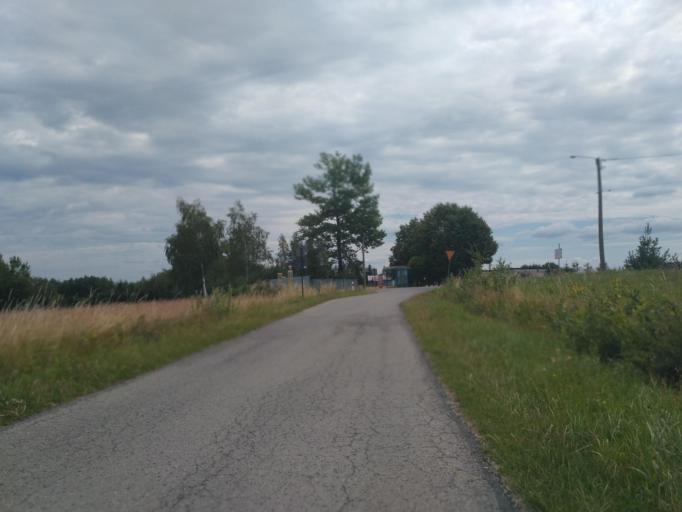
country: PL
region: Subcarpathian Voivodeship
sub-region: Powiat rzeszowski
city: Straszydle
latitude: 49.8820
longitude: 21.9866
